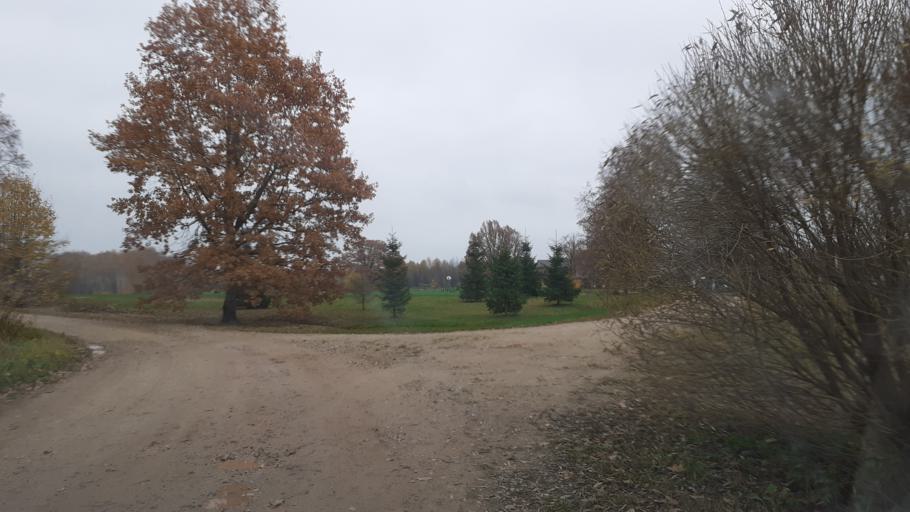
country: LV
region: Saldus Rajons
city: Saldus
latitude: 56.8597
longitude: 22.3401
